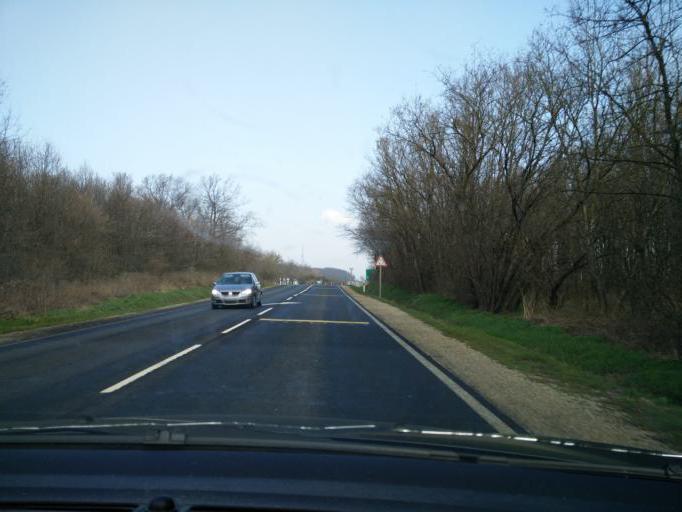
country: HU
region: Somogy
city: Balatonbereny
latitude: 46.6773
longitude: 17.3409
